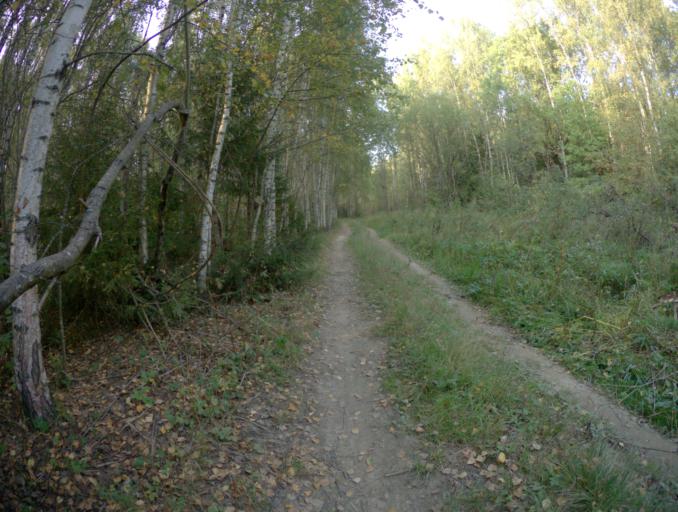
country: RU
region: Vladimir
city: Golovino
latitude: 55.9992
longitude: 40.4483
